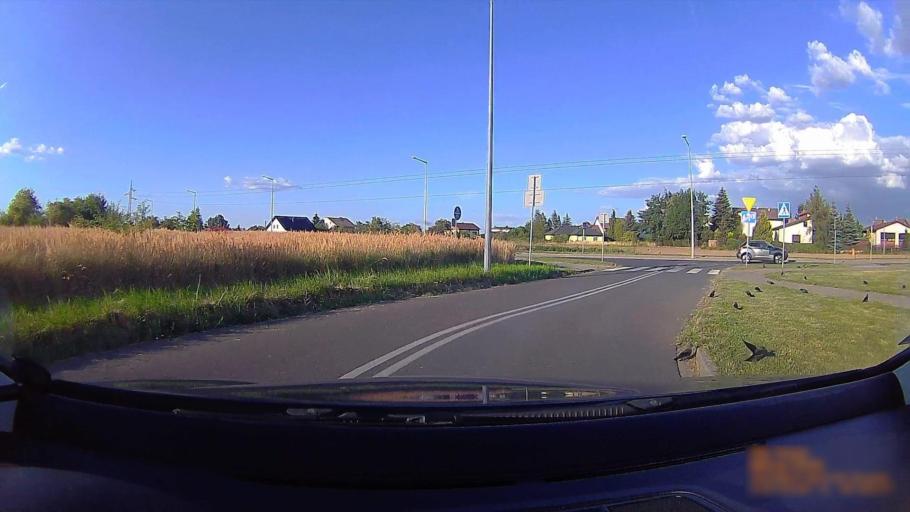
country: PL
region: Greater Poland Voivodeship
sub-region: Konin
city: Konin
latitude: 52.2007
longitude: 18.2393
